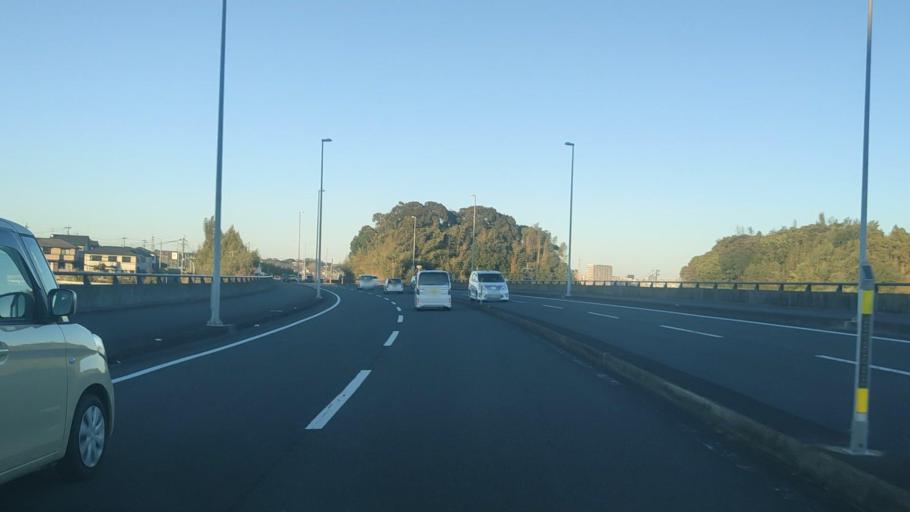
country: JP
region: Miyazaki
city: Miyazaki-shi
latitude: 31.8871
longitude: 131.4021
